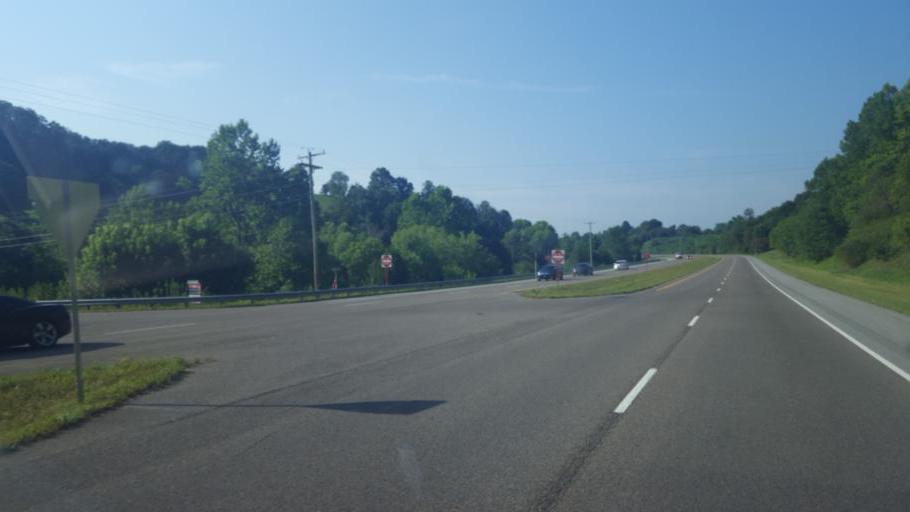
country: US
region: Tennessee
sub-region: Carter County
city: Elizabethton
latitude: 36.3904
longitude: -82.2274
